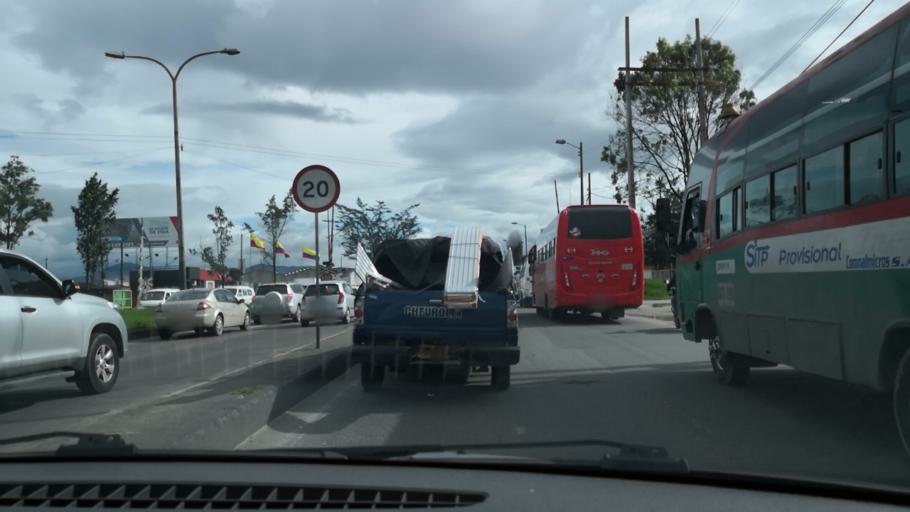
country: CO
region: Bogota D.C.
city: Bogota
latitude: 4.6457
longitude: -74.1100
